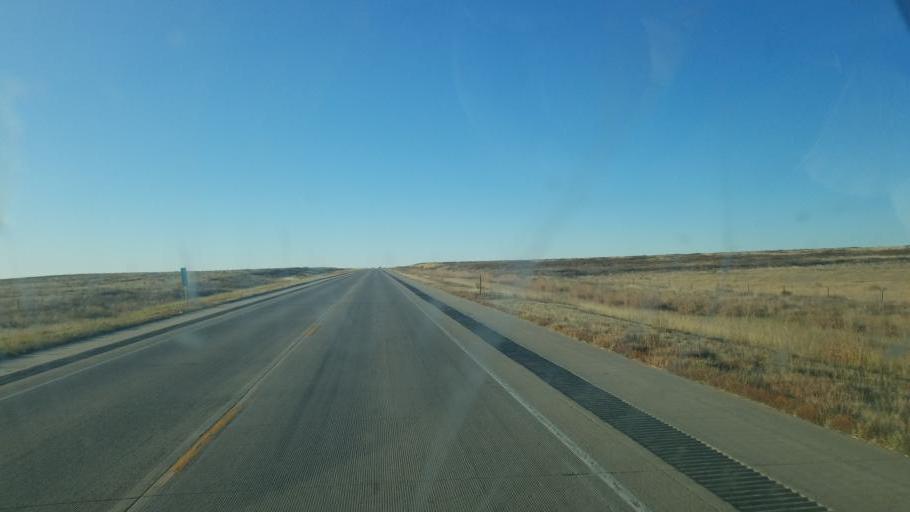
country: US
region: Colorado
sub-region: Kiowa County
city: Eads
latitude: 38.7049
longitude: -102.7758
